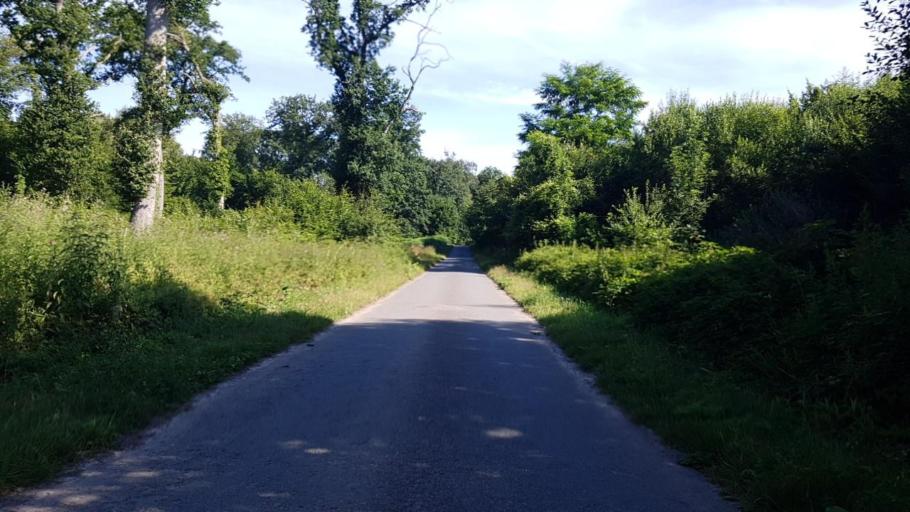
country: FR
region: Picardie
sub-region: Departement de l'Oise
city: Fleurines
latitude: 49.2609
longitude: 2.6192
